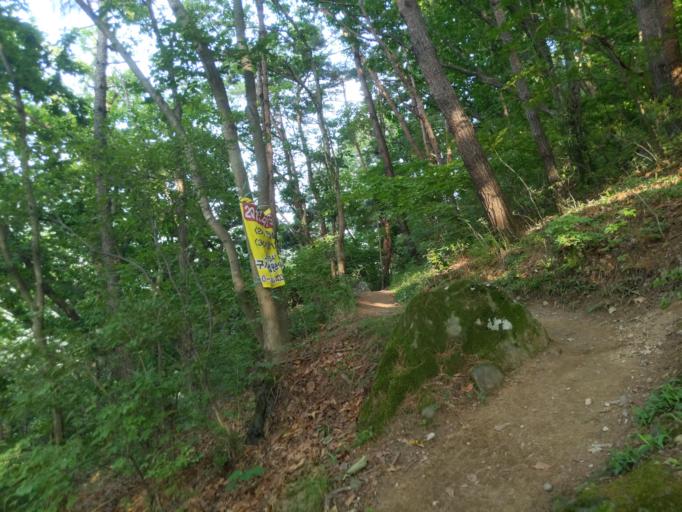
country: KR
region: Daegu
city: Hwawon
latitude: 35.7867
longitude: 128.5454
